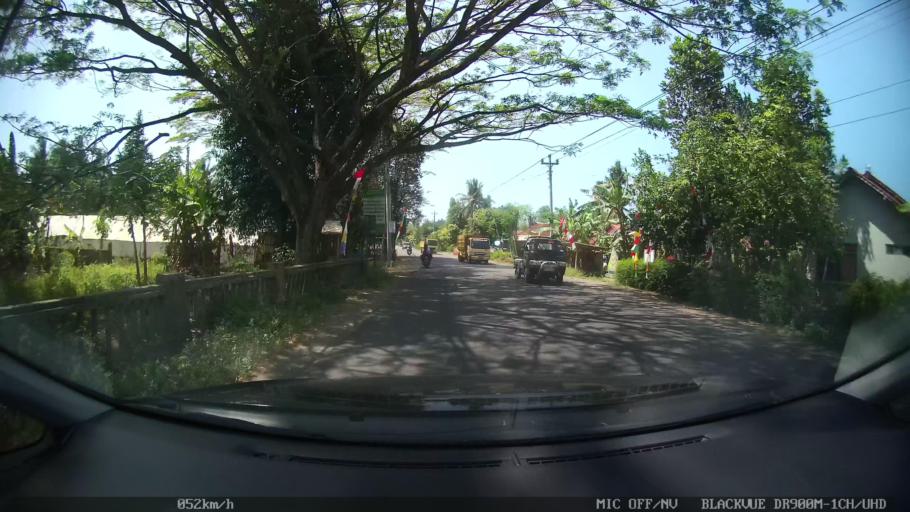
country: ID
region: Daerah Istimewa Yogyakarta
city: Srandakan
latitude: -7.9046
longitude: 110.0767
